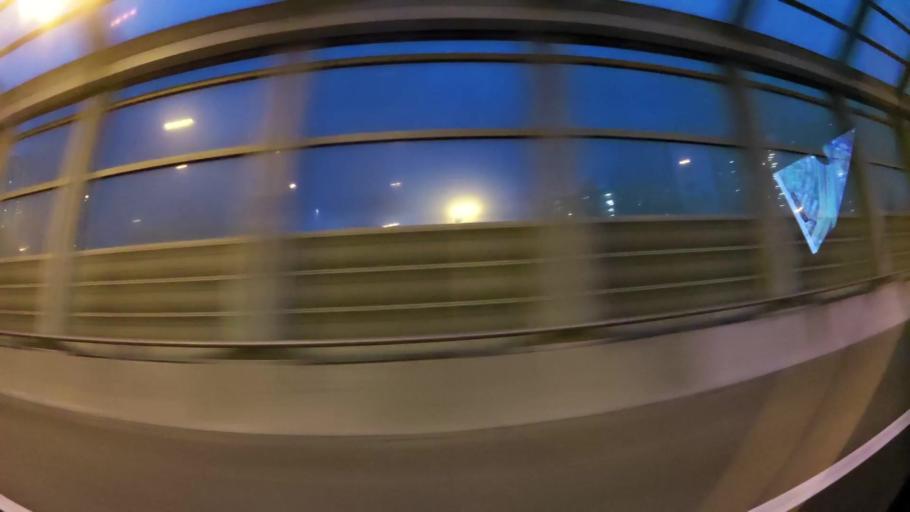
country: HK
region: Sha Tin
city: Sha Tin
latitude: 22.3765
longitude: 114.1762
